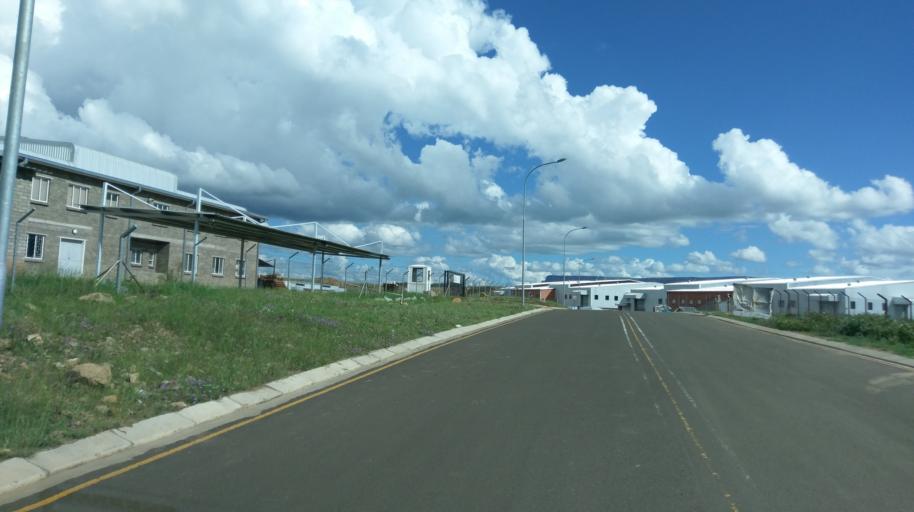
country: LS
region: Maseru
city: Maseru
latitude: -29.3808
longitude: 27.4842
